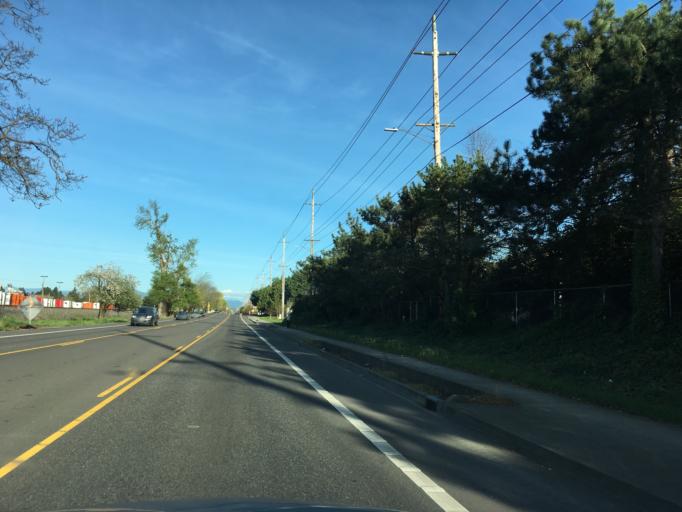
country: US
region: Oregon
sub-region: Multnomah County
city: Lents
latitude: 45.5563
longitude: -122.5325
